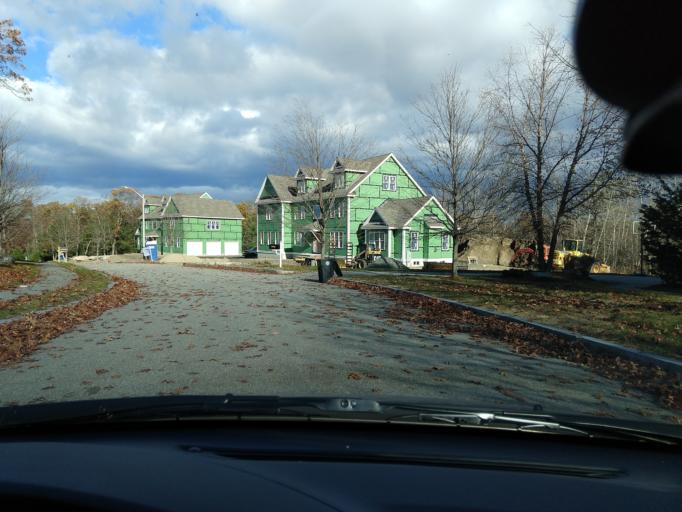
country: US
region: Massachusetts
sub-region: Middlesex County
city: Pinehurst
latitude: 42.4947
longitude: -71.2396
